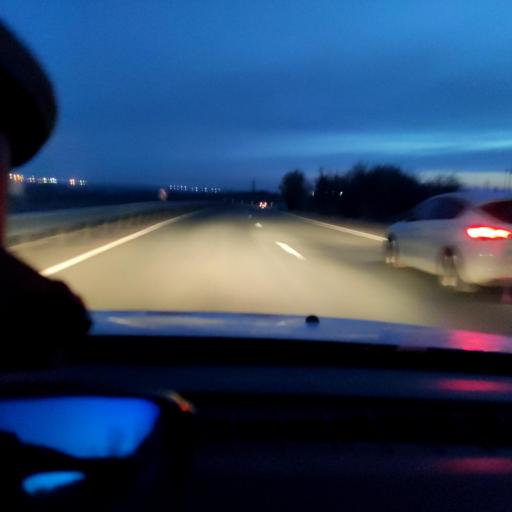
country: RU
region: Samara
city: Novokuybyshevsk
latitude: 53.0208
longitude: 49.9835
